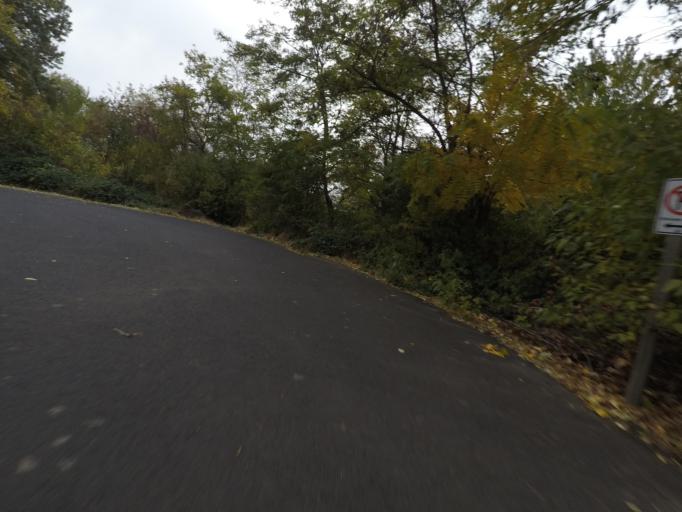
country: US
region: Washington
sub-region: Walla Walla County
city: Walla Walla East
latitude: 46.0815
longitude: -118.2569
